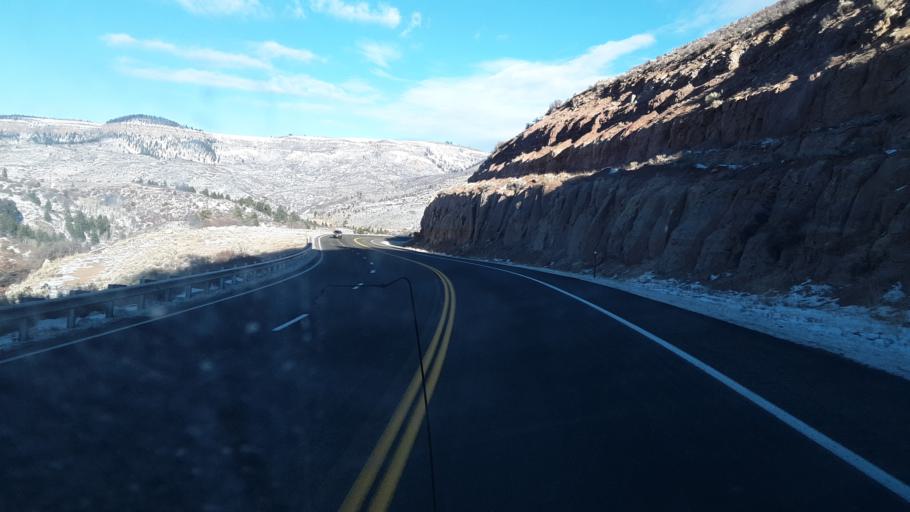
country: US
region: Colorado
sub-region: Hinsdale County
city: Lake City
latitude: 38.4417
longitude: -107.3404
